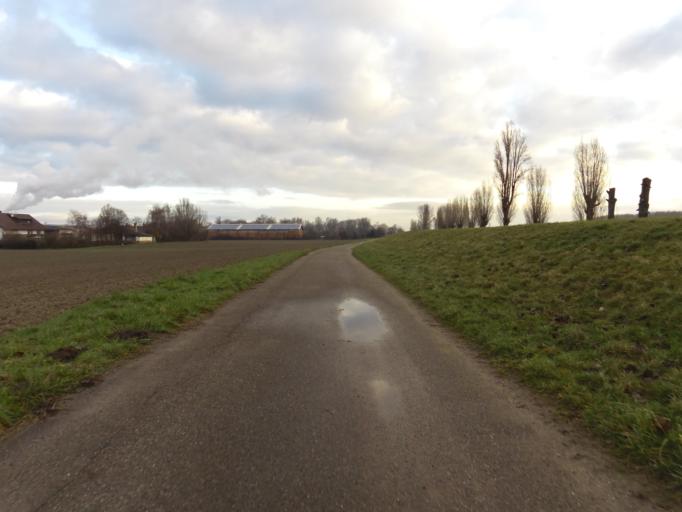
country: DE
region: Rheinland-Pfalz
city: Bobenheim-Roxheim
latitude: 49.5676
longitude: 8.4148
